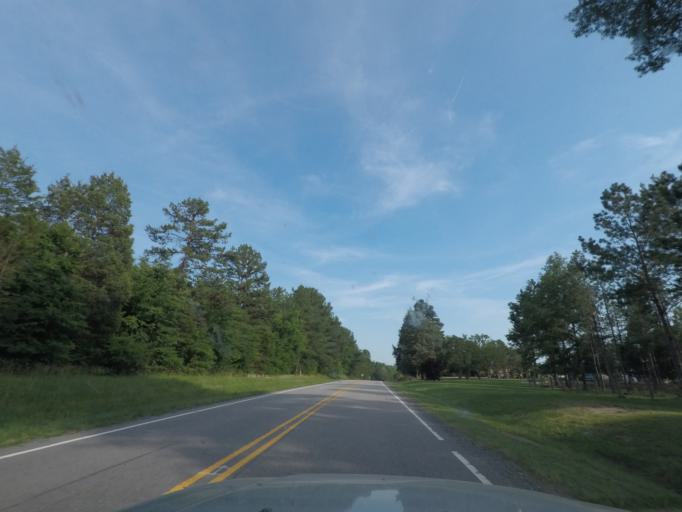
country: US
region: Virginia
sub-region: Mecklenburg County
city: Clarksville
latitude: 36.5352
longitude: -78.5374
